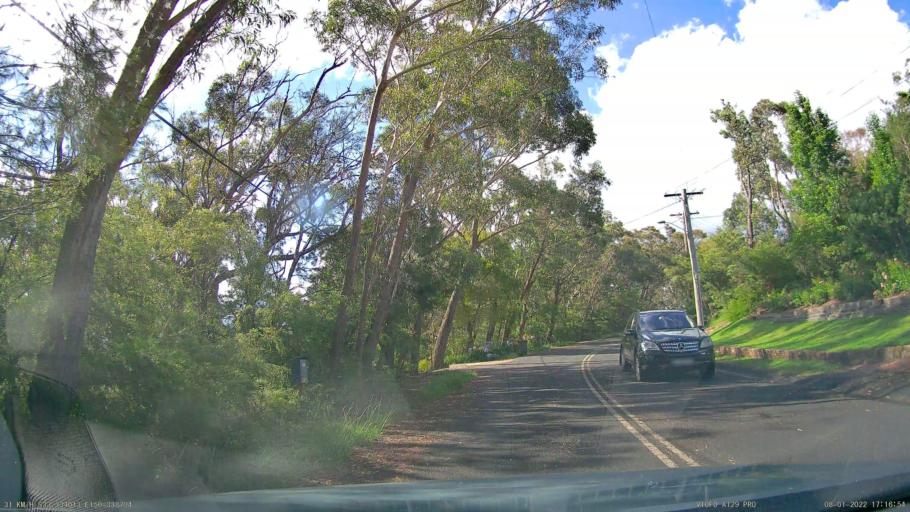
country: AU
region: New South Wales
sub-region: Blue Mountains Municipality
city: Leura
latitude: -33.7339
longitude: 150.3386
